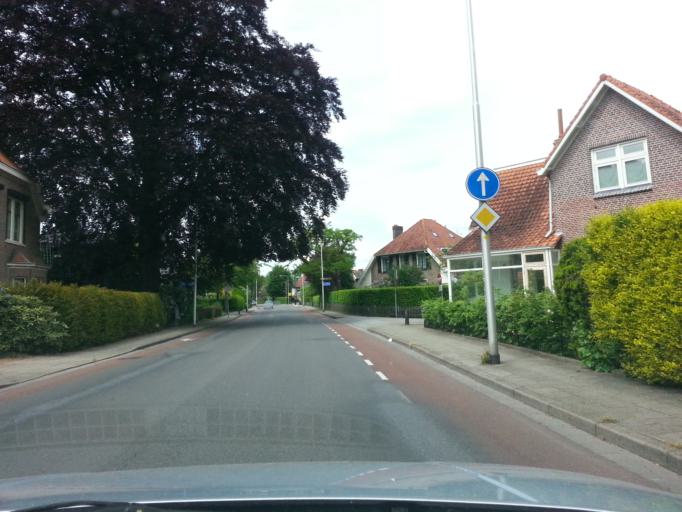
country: NL
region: Gelderland
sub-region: Gemeente Lochem
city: Lochem
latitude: 52.1542
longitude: 6.4181
